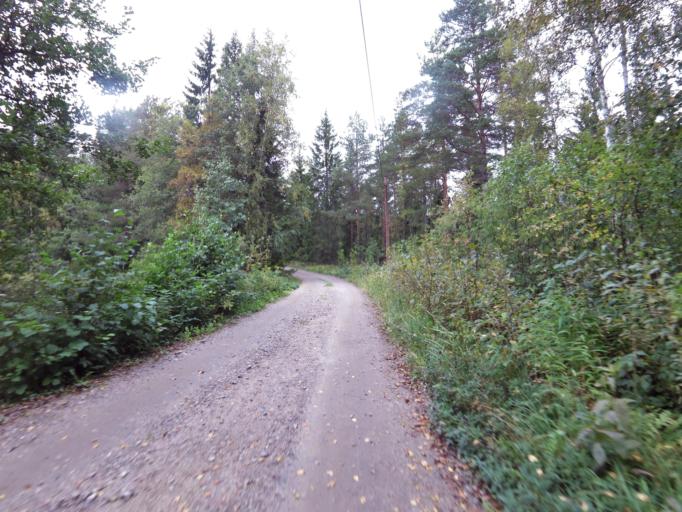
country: SE
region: Gaevleborg
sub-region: Gavle Kommun
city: Valbo
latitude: 60.7554
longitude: 16.9672
